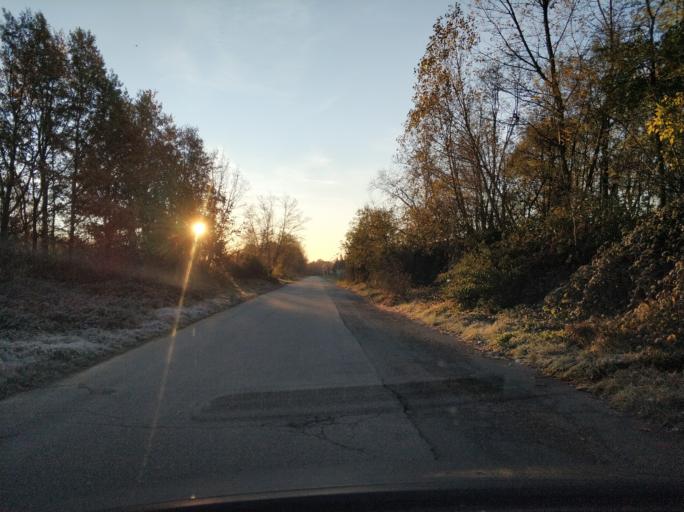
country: IT
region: Piedmont
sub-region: Provincia di Torino
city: Robassomero
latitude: 45.1809
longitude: 7.5981
